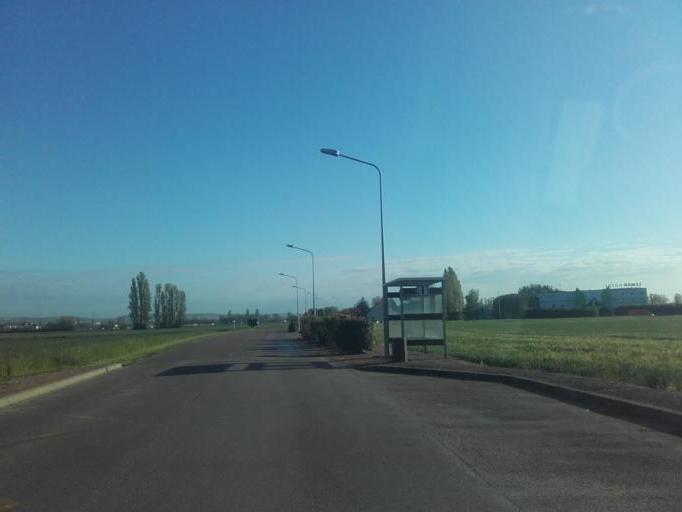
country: FR
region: Bourgogne
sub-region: Departement de la Cote-d'Or
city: Bligny-les-Beaune
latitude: 46.9958
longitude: 4.8516
